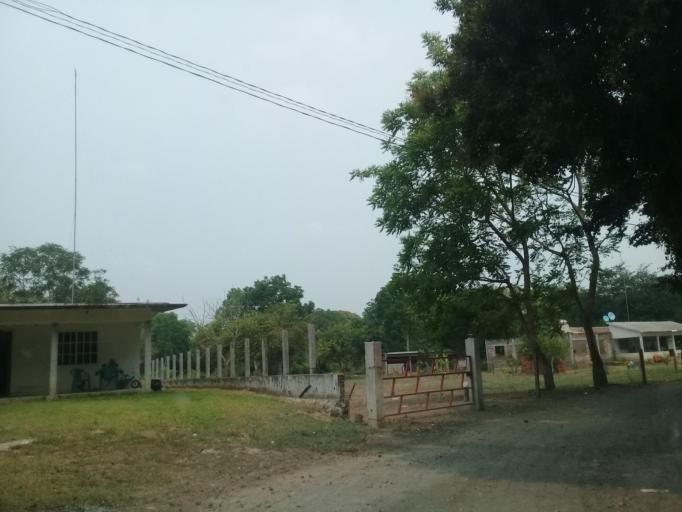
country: MX
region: Veracruz
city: Jamapa
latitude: 18.9520
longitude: -96.2054
